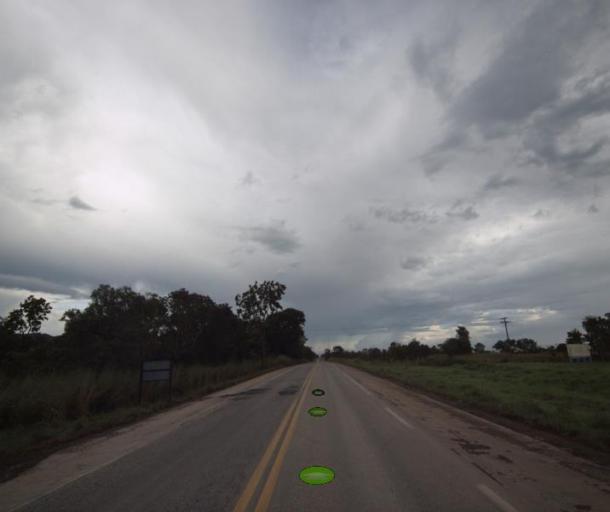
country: BR
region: Goias
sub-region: Porangatu
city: Porangatu
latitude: -13.5985
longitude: -49.0419
